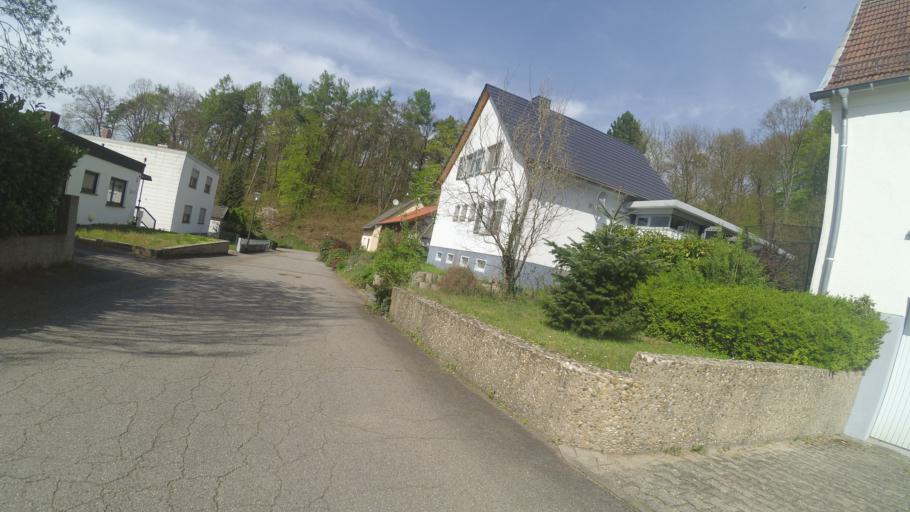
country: DE
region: Saarland
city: Homburg
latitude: 49.3352
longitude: 7.3699
